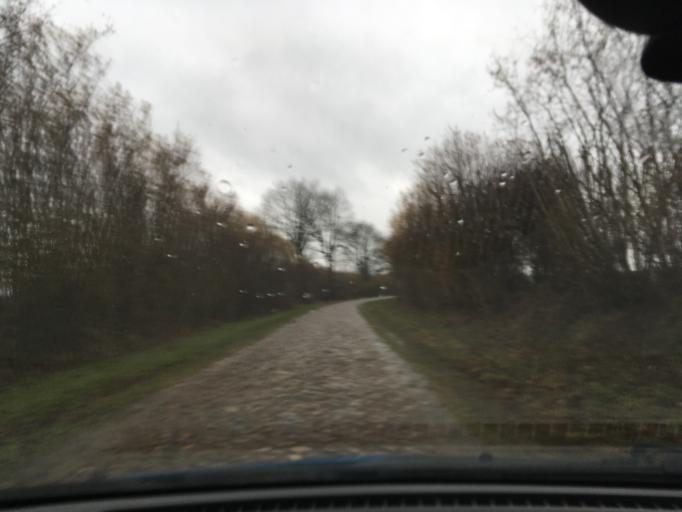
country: DE
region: Schleswig-Holstein
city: Schnakenbek
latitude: 53.3937
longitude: 10.5072
